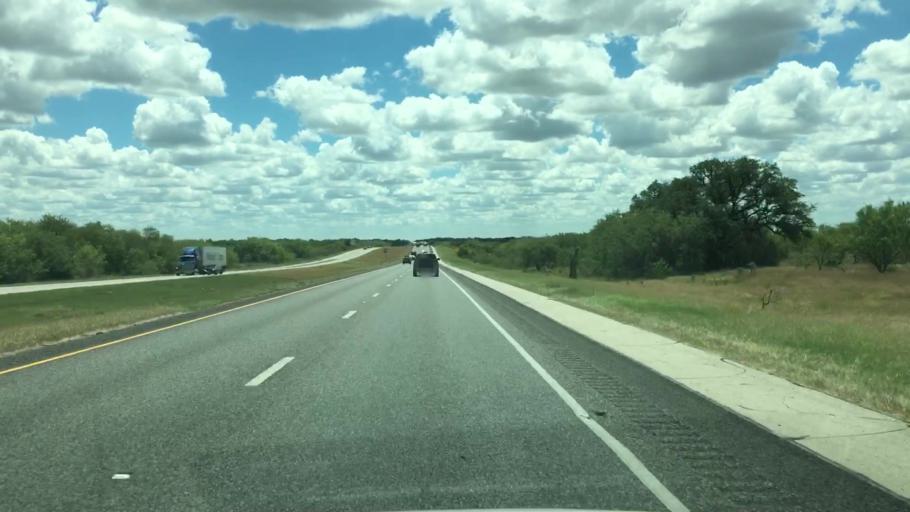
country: US
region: Texas
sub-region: Atascosa County
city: Pleasanton
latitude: 29.0923
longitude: -98.4331
